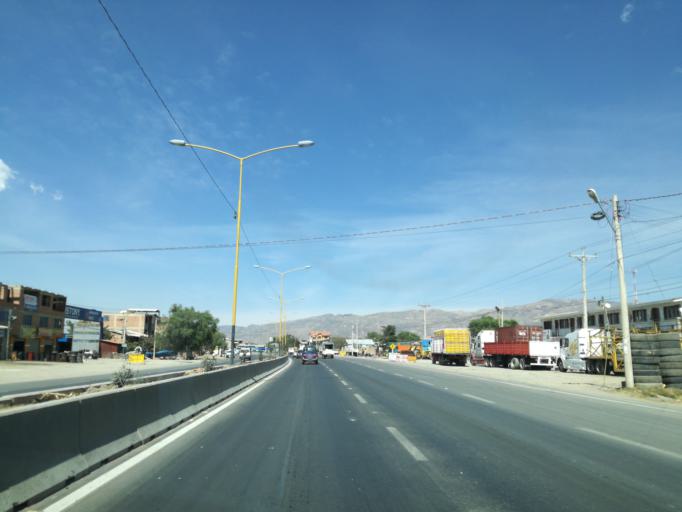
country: BO
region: Cochabamba
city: Sipe Sipe
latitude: -17.4104
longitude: -66.3326
